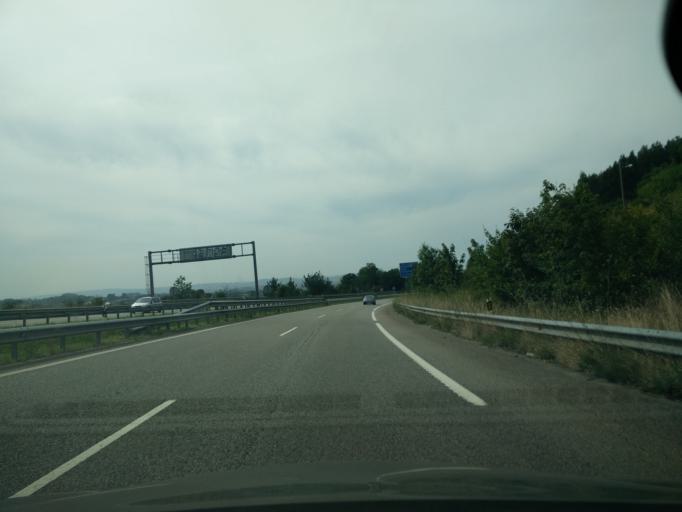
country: ES
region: Asturias
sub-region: Province of Asturias
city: Arriba
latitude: 43.5043
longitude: -5.5918
